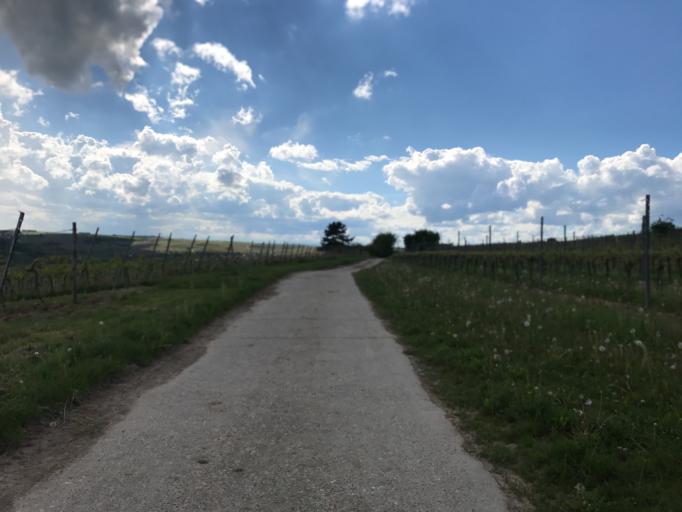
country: DE
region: Rheinland-Pfalz
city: Stadecken-Elsheim
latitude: 49.9252
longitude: 8.1231
